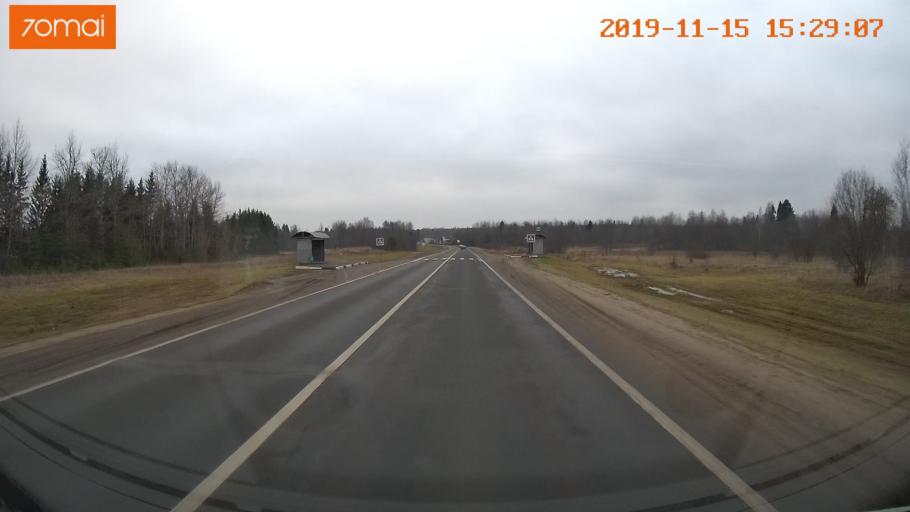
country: RU
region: Jaroslavl
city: Danilov
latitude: 58.1243
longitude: 40.1245
